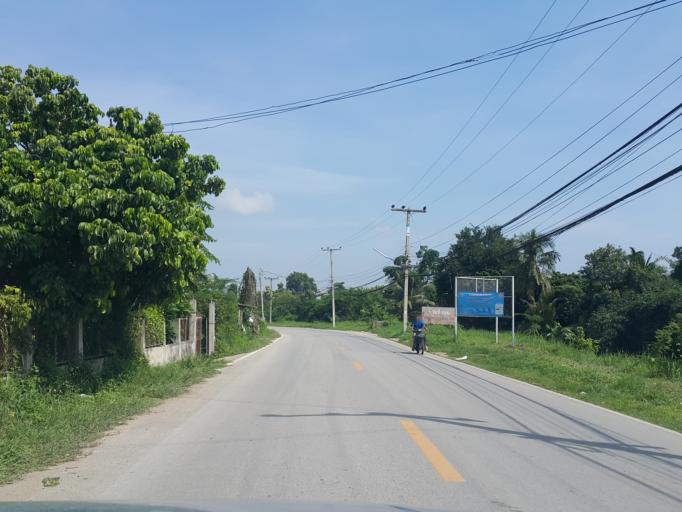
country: TH
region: Chiang Mai
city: Saraphi
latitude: 18.6877
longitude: 99.0607
